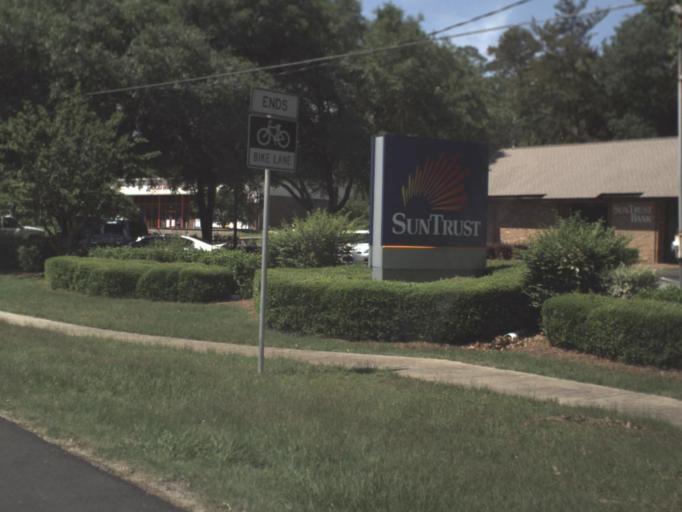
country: US
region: Florida
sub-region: Jackson County
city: Marianna
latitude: 30.7838
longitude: -85.2265
